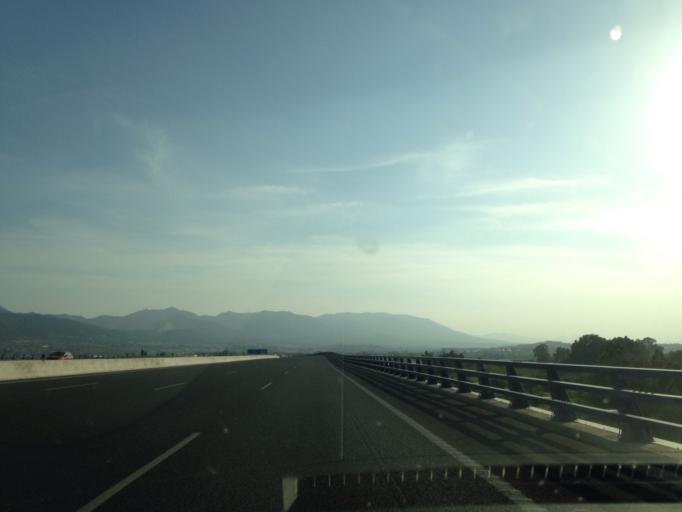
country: ES
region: Andalusia
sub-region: Provincia de Malaga
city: Alhaurin de la Torre
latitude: 36.6963
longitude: -4.5203
